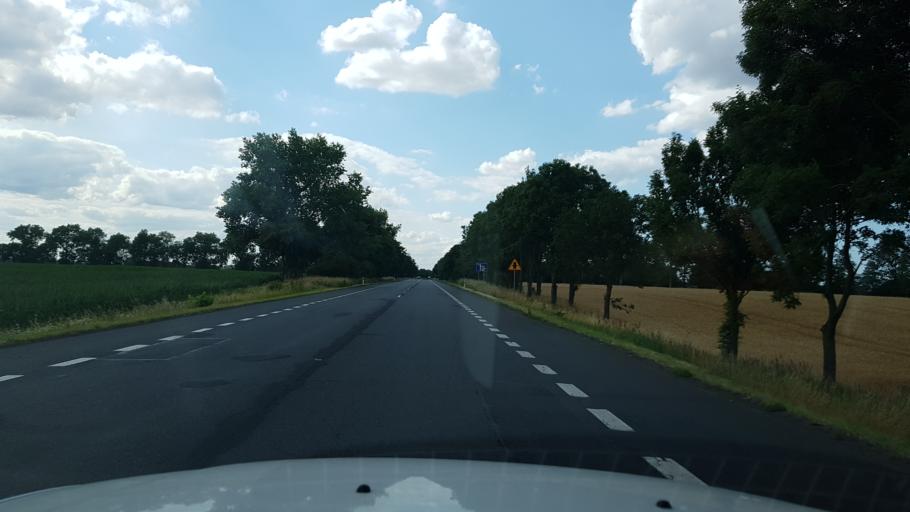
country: PL
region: West Pomeranian Voivodeship
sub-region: Powiat pyrzycki
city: Pyrzyce
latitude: 53.1947
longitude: 14.8299
